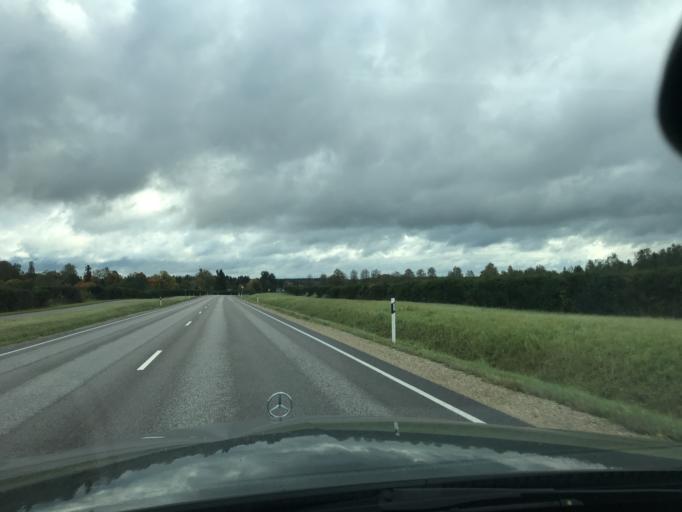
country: EE
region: Valgamaa
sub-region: Torva linn
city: Torva
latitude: 58.0086
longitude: 25.9049
